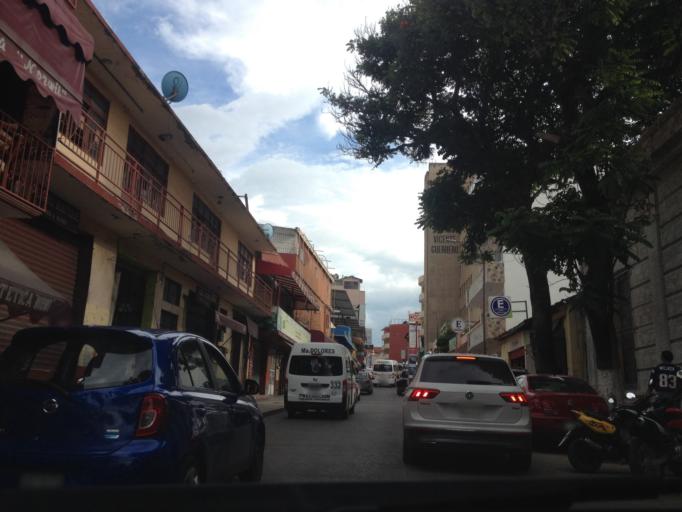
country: MX
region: Guerrero
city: Chilpancingo de los Bravos
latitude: 17.5539
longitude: -99.5032
